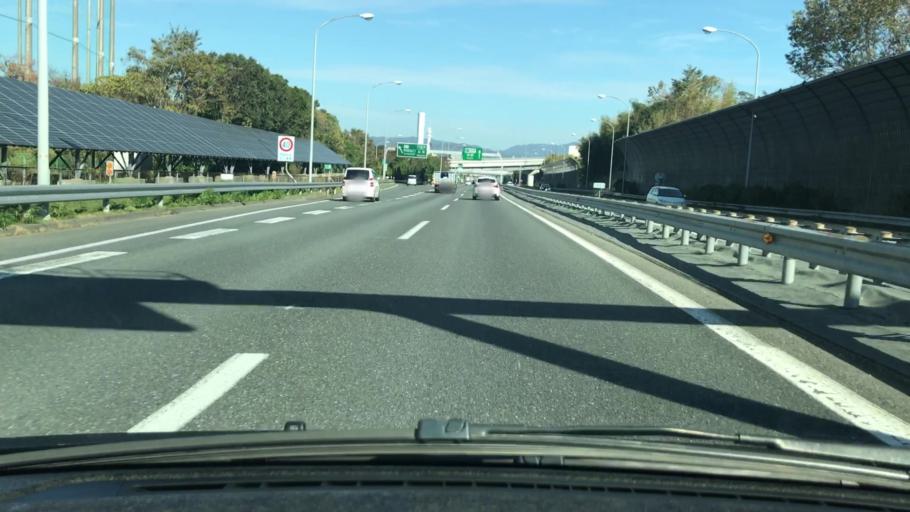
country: JP
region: Osaka
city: Ibaraki
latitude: 34.7998
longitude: 135.5399
